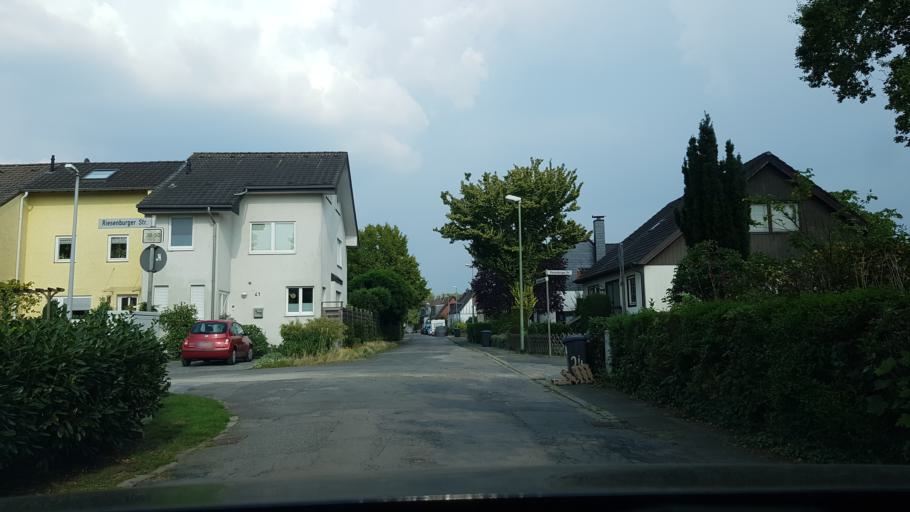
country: DE
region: North Rhine-Westphalia
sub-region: Regierungsbezirk Dusseldorf
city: Hochfeld
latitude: 51.3894
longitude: 6.7880
